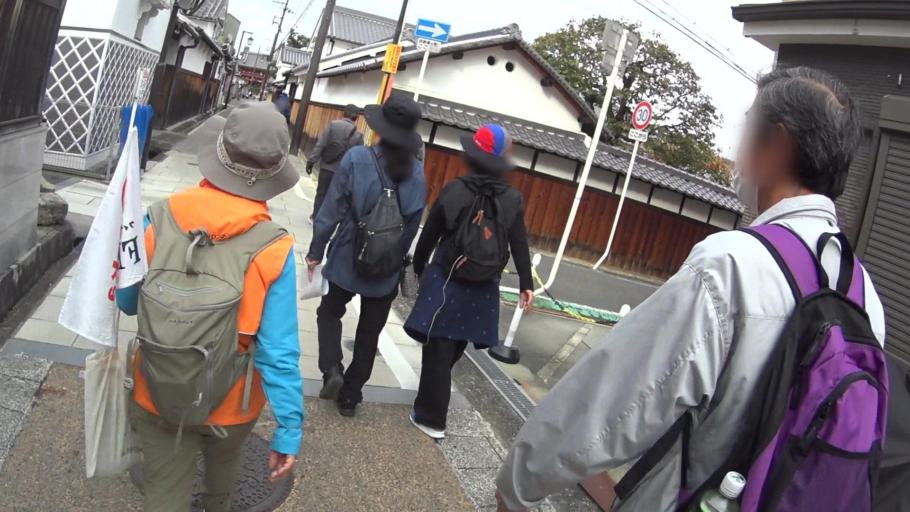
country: JP
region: Osaka
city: Kashihara
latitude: 34.5679
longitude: 135.5967
